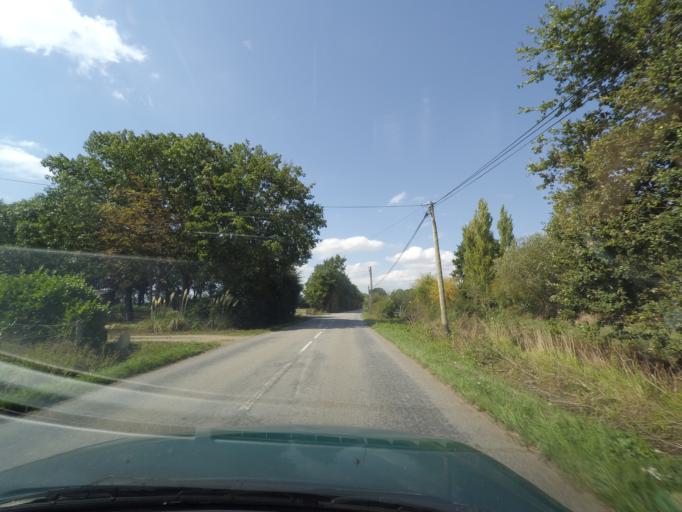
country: FR
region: Pays de la Loire
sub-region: Departement de la Loire-Atlantique
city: Saint-Lumine-de-Coutais
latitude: 47.0679
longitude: -1.7713
